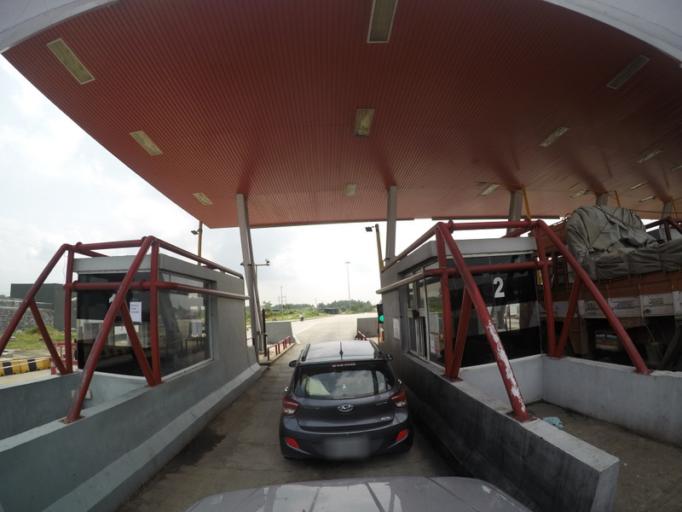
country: IN
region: Karnataka
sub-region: Mandya
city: Belluru
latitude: 12.9582
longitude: 76.6236
